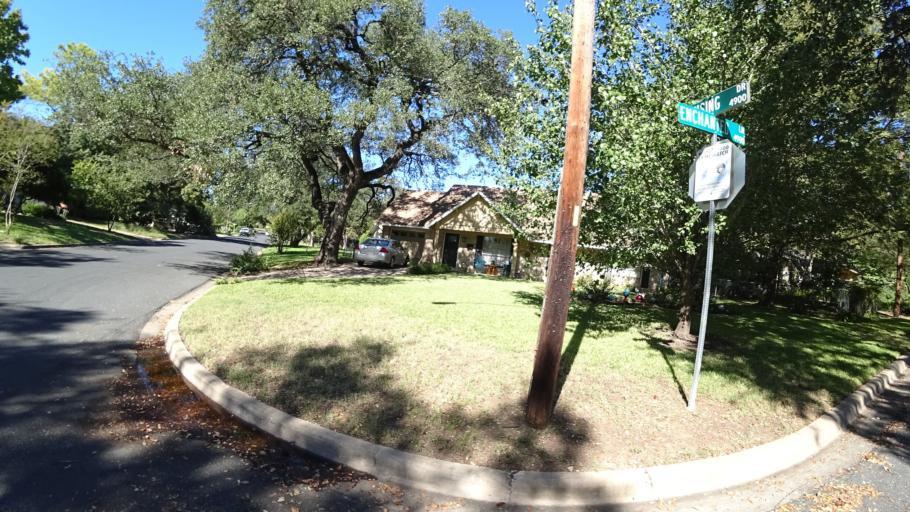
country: US
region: Texas
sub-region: Travis County
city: Rollingwood
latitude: 30.2215
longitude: -97.7914
